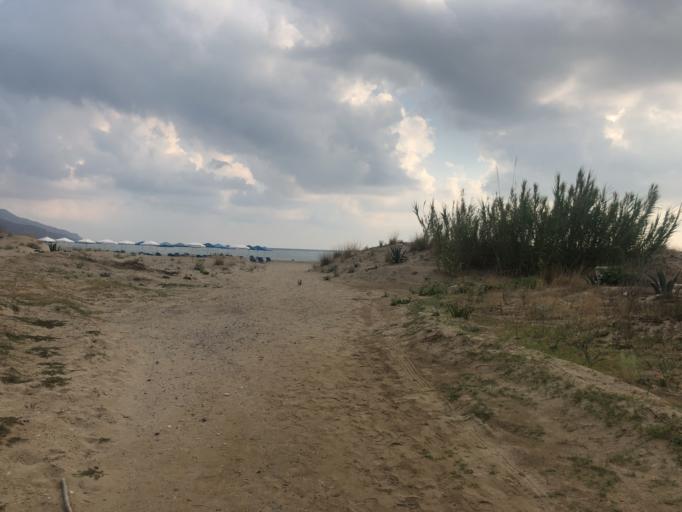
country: GR
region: Crete
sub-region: Nomos Chanias
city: Georgioupolis
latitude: 35.3560
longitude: 24.2775
